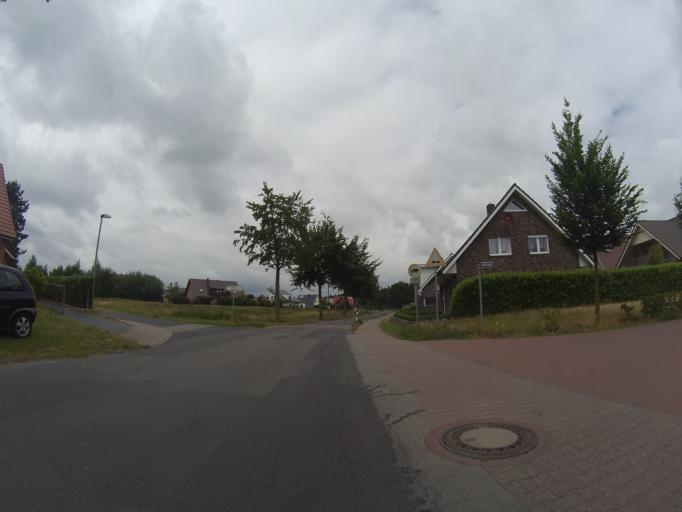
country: DE
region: Lower Saxony
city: Meppen
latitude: 52.6942
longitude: 7.2588
